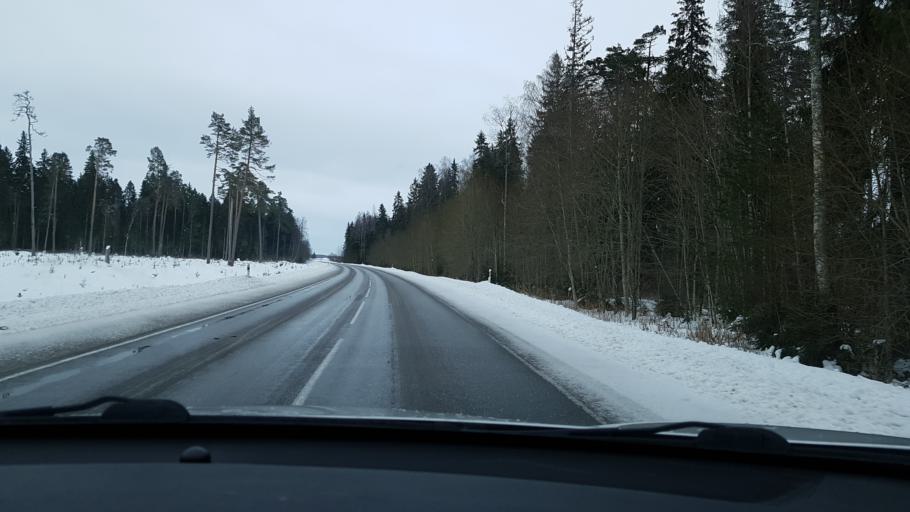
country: EE
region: Jaervamaa
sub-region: Jaerva-Jaani vald
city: Jarva-Jaani
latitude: 59.0971
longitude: 25.8202
